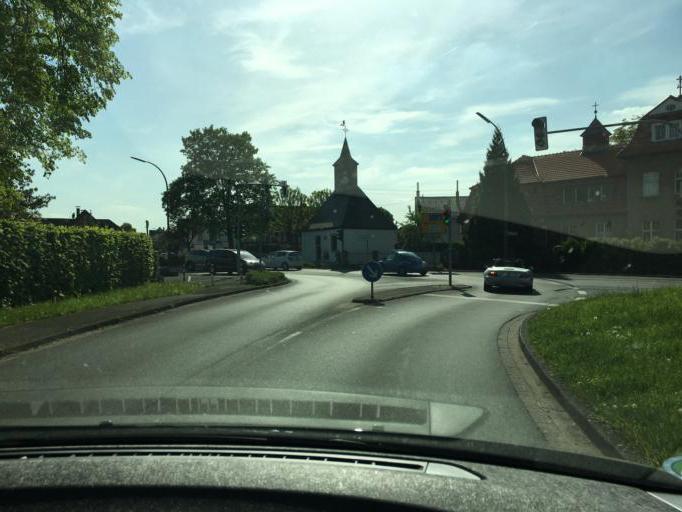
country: DE
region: North Rhine-Westphalia
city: Wesseling
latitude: 50.7904
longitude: 6.9570
